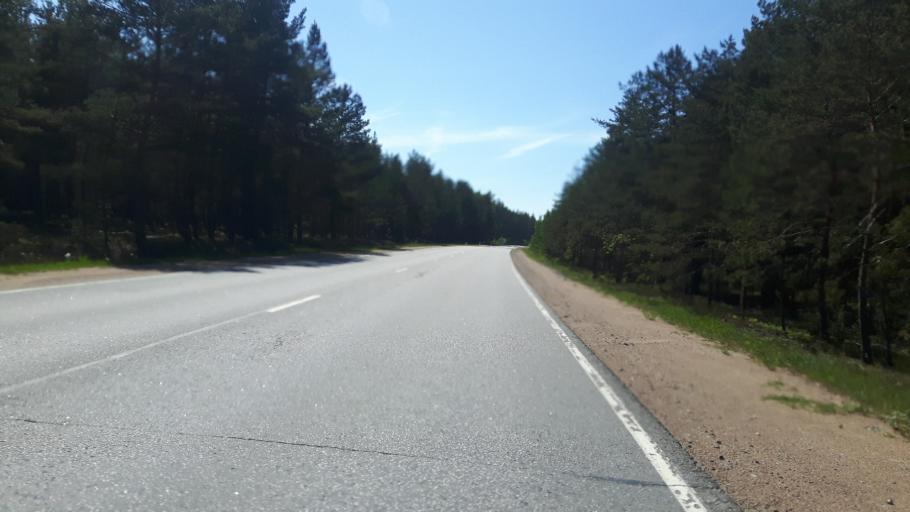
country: RU
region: Leningrad
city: Sista-Palkino
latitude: 59.7669
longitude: 28.7459
